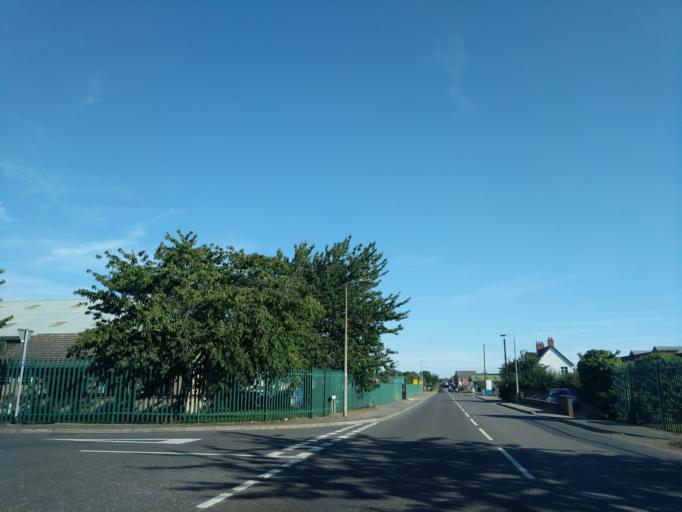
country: GB
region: England
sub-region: Lincolnshire
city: Bourne
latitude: 52.7626
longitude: -0.3624
